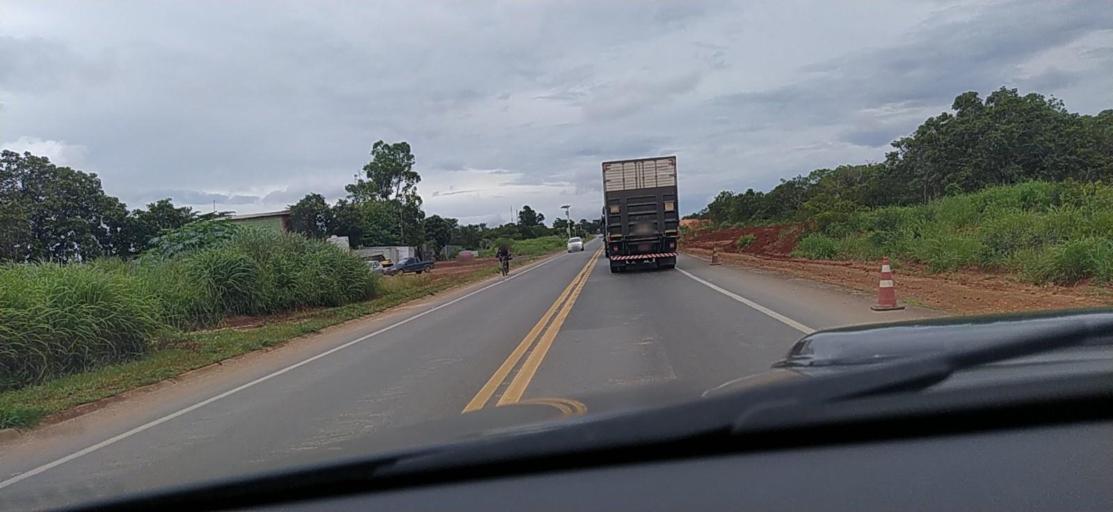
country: BR
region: Minas Gerais
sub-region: Curvelo
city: Curvelo
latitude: -18.7169
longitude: -44.4424
